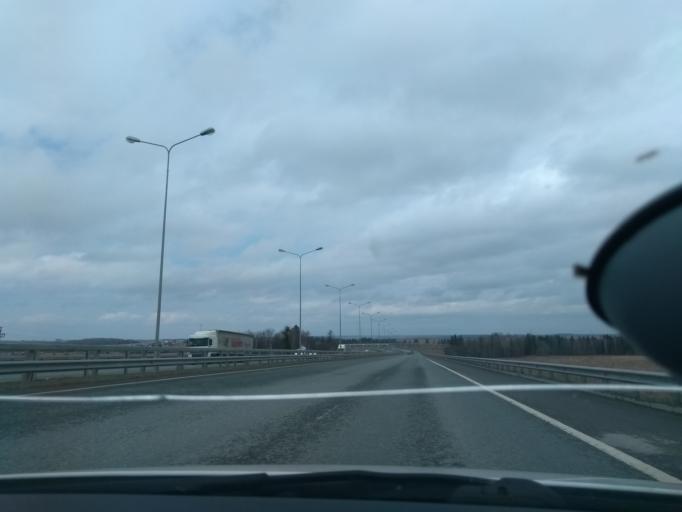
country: RU
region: Perm
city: Zvezdnyy
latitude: 57.7736
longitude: 56.3380
